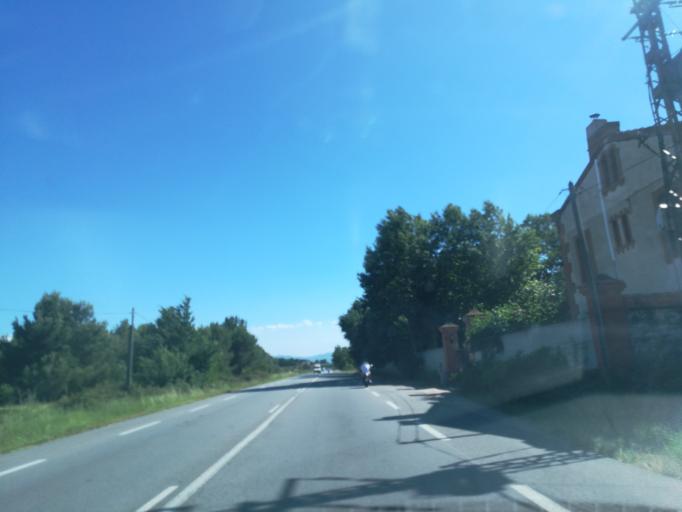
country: FR
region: Languedoc-Roussillon
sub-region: Departement des Pyrenees-Orientales
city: Pollestres
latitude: 42.6135
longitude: 2.8631
